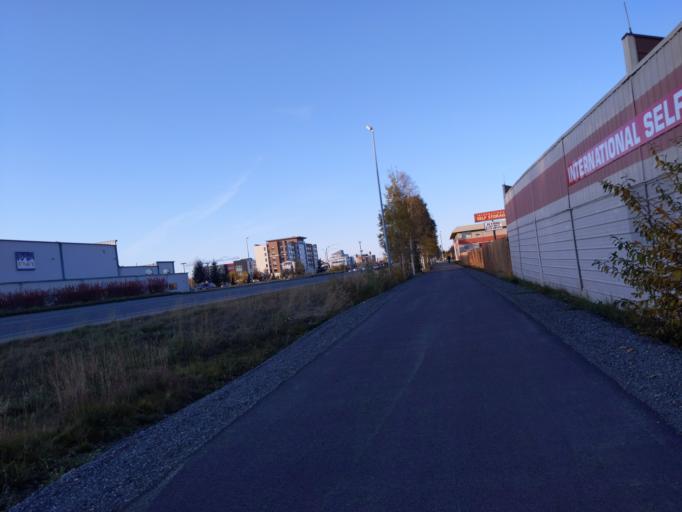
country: US
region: Alaska
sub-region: Anchorage Municipality
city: Anchorage
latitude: 61.1715
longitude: -149.8858
